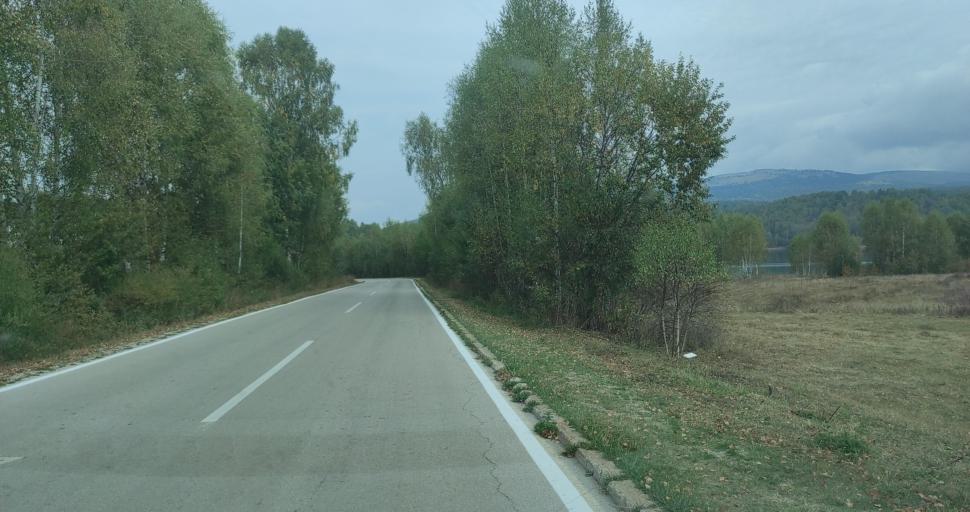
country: RS
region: Central Serbia
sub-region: Jablanicki Okrug
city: Crna Trava
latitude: 42.7366
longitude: 22.3309
